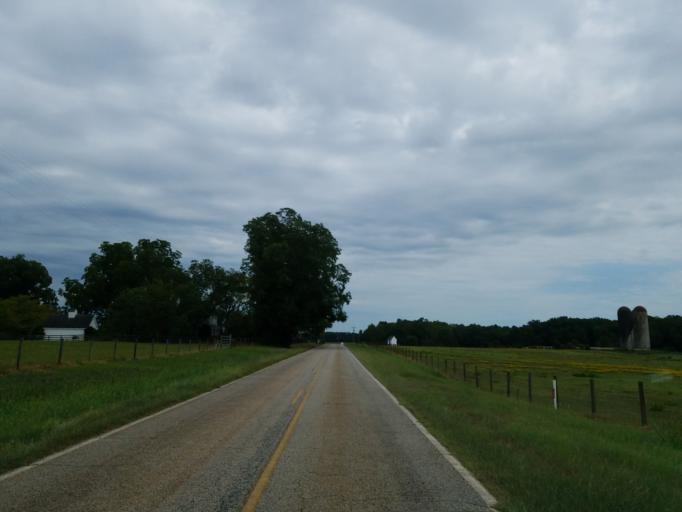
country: US
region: Georgia
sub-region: Lamar County
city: Barnesville
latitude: 32.9985
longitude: -84.0537
